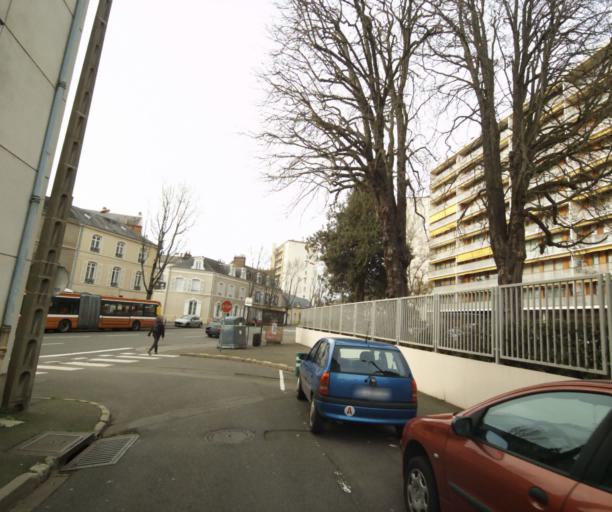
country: FR
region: Pays de la Loire
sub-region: Departement de la Sarthe
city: Le Mans
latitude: 48.0004
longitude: 0.2122
